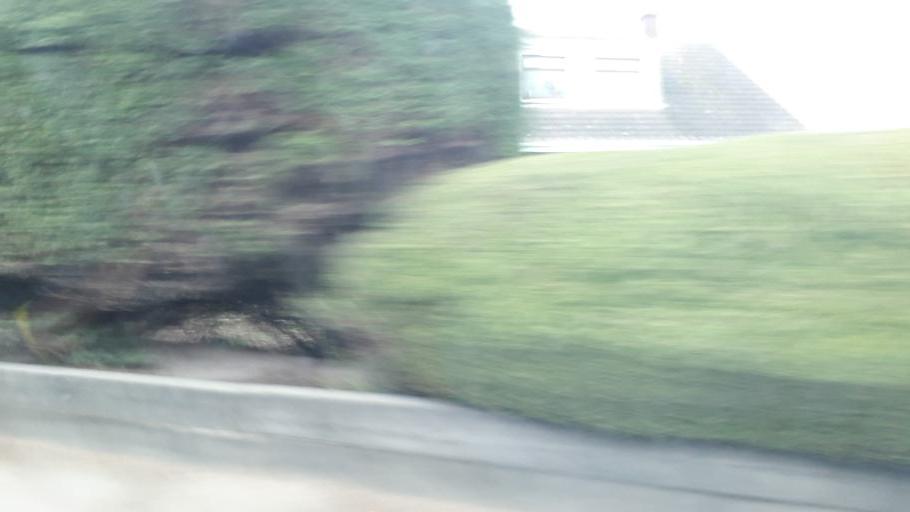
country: IE
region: Leinster
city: An Ros
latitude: 53.5195
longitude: -6.1153
